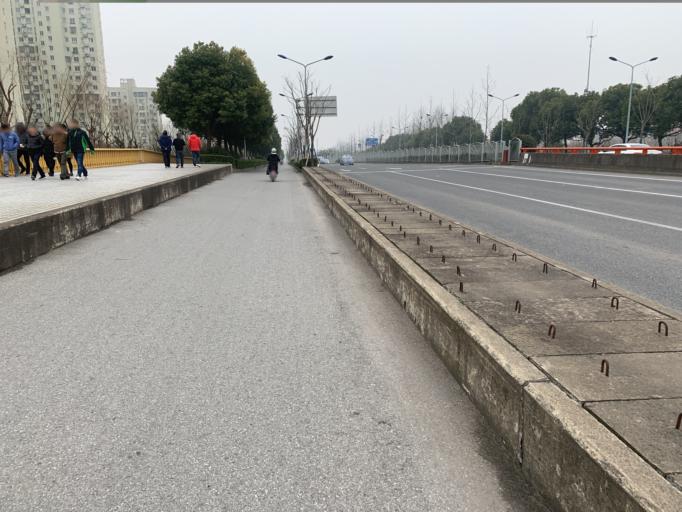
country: CN
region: Shanghai Shi
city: Huamu
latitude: 31.2438
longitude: 121.6212
